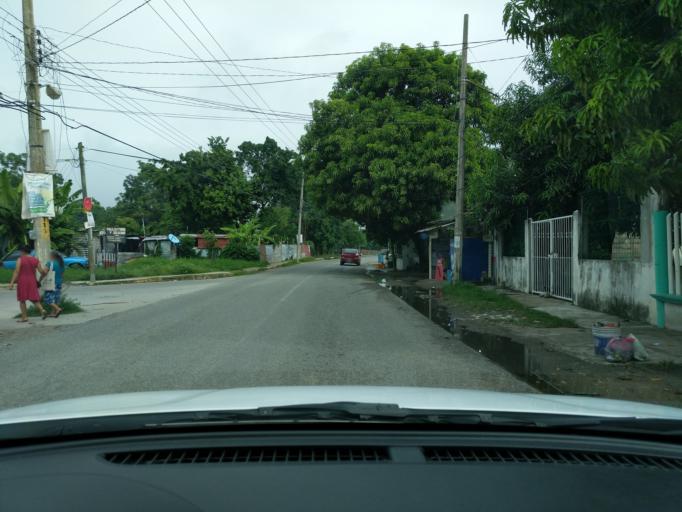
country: MX
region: Tabasco
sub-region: Centro
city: La Lima
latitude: 17.9498
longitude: -92.9646
